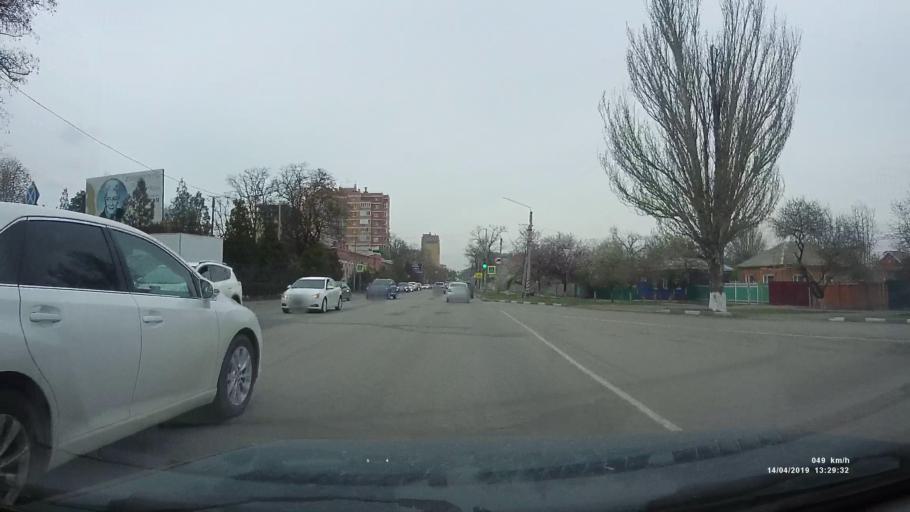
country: RU
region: Rostov
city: Azov
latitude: 47.1033
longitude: 39.4355
